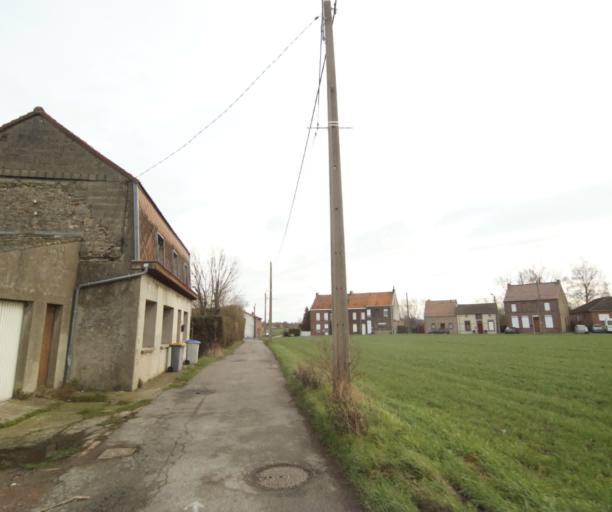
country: BE
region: Wallonia
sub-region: Province du Hainaut
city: Peruwelz
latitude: 50.4942
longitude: 3.5782
